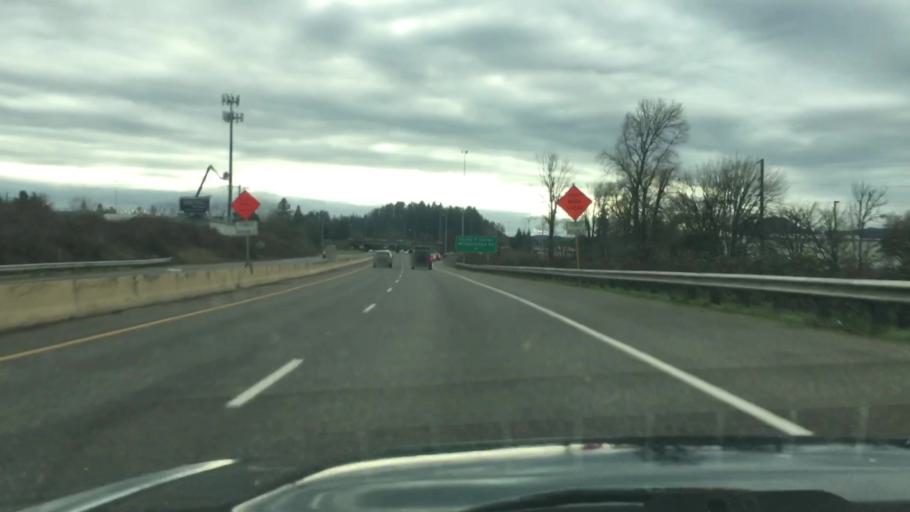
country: US
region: Oregon
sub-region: Lane County
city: Eugene
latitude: 44.0747
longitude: -123.1051
